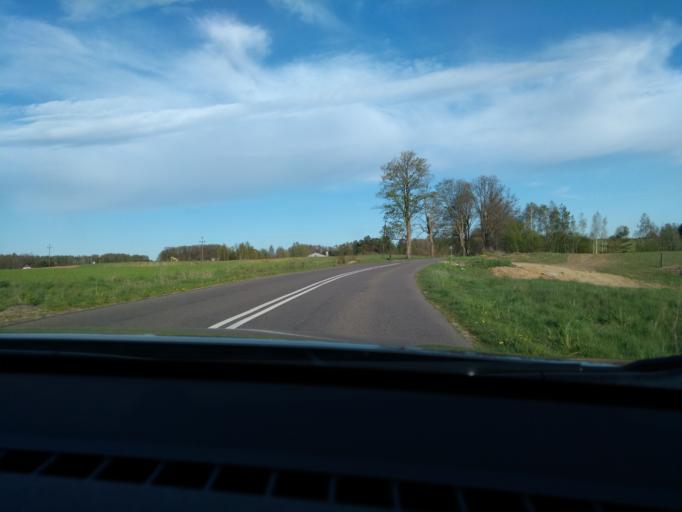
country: PL
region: Pomeranian Voivodeship
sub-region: Powiat leborski
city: Cewice
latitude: 54.3400
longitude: 17.7564
